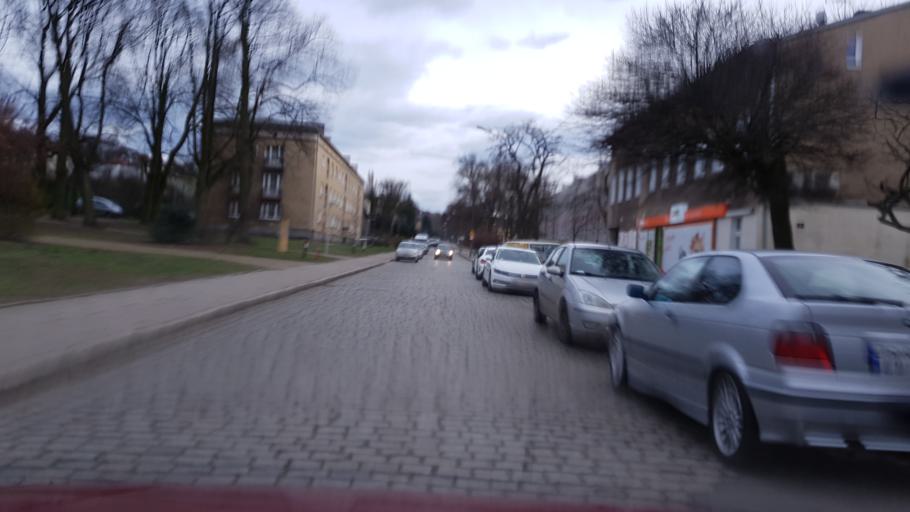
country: PL
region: West Pomeranian Voivodeship
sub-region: Szczecin
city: Szczecin
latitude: 53.3661
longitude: 14.5987
